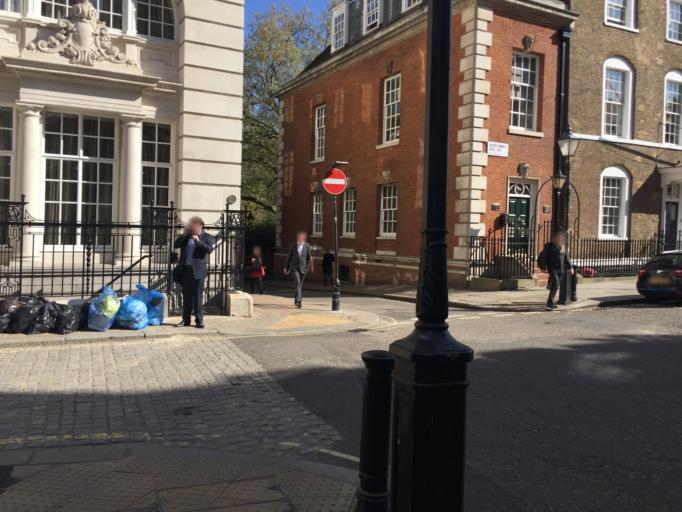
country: GB
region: England
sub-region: Greater London
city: London
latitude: 51.5004
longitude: -0.1339
